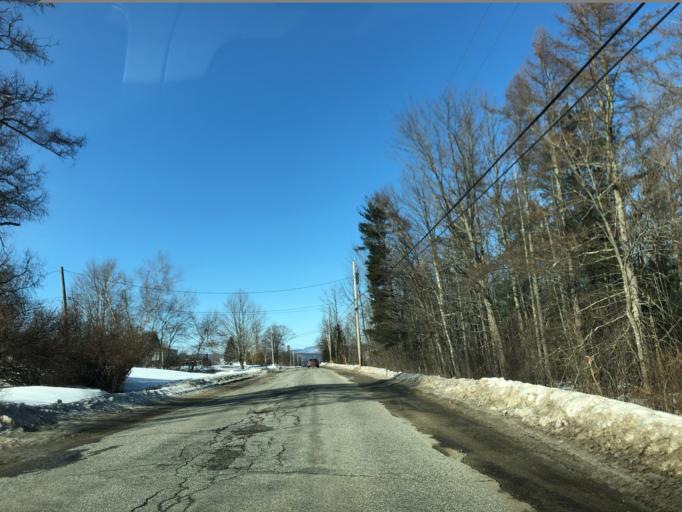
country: US
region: Maine
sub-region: Oxford County
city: Buckfield
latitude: 44.2673
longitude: -70.3502
